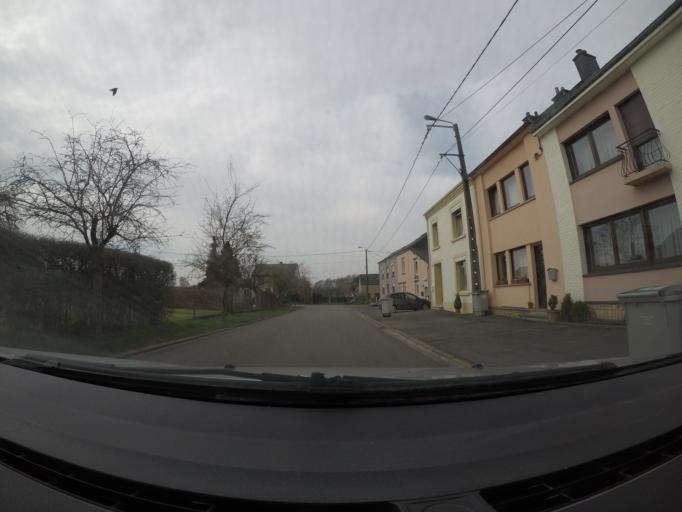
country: BE
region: Wallonia
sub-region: Province du Luxembourg
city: Tintigny
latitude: 49.7235
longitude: 5.5331
